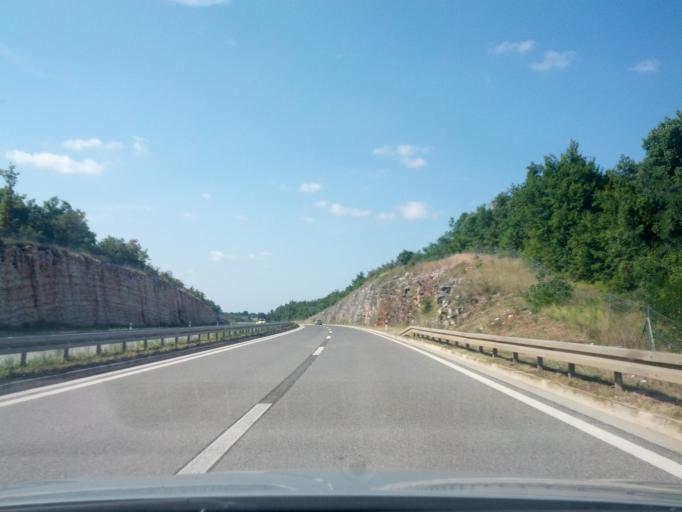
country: HR
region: Istarska
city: Buje
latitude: 45.3887
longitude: 13.6169
